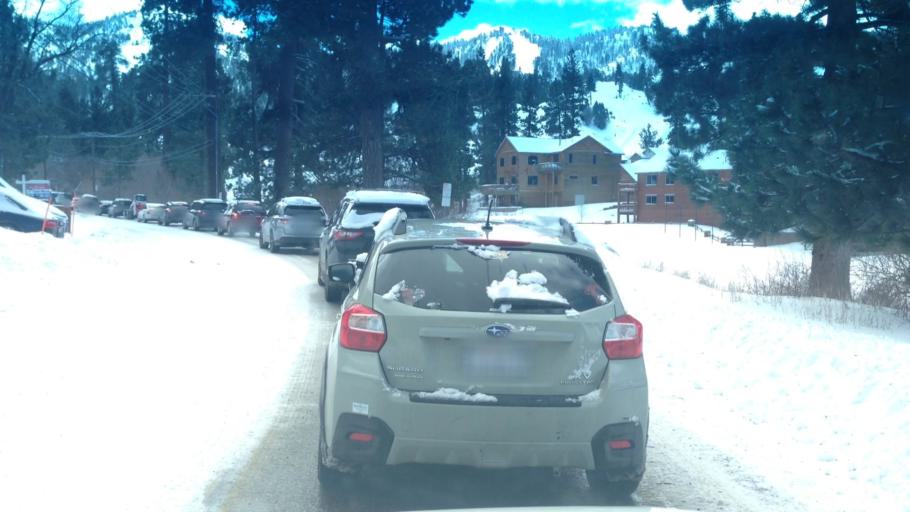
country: US
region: California
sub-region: San Bernardino County
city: Big Bear City
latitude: 34.2322
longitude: -116.8606
